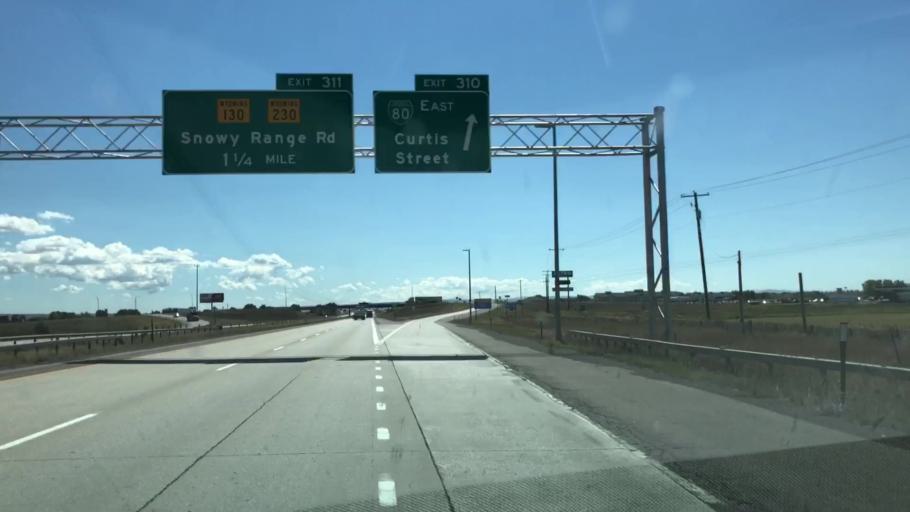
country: US
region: Wyoming
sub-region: Albany County
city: Laramie
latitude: 41.3324
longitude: -105.6164
